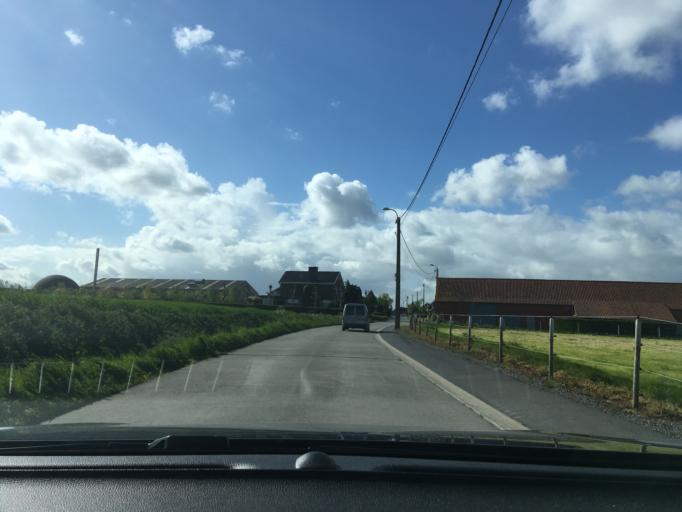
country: BE
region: Flanders
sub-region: Provincie West-Vlaanderen
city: Hooglede
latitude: 50.9996
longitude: 3.0773
